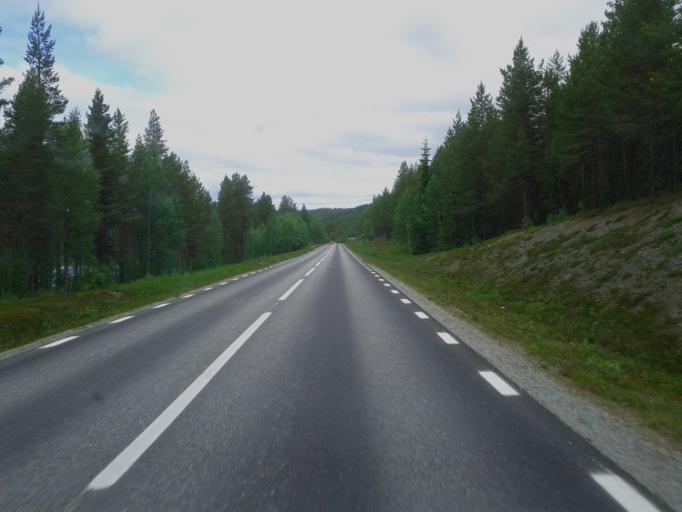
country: SE
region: Vaesterbotten
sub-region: Storumans Kommun
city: Fristad
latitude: 65.3740
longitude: 16.5163
